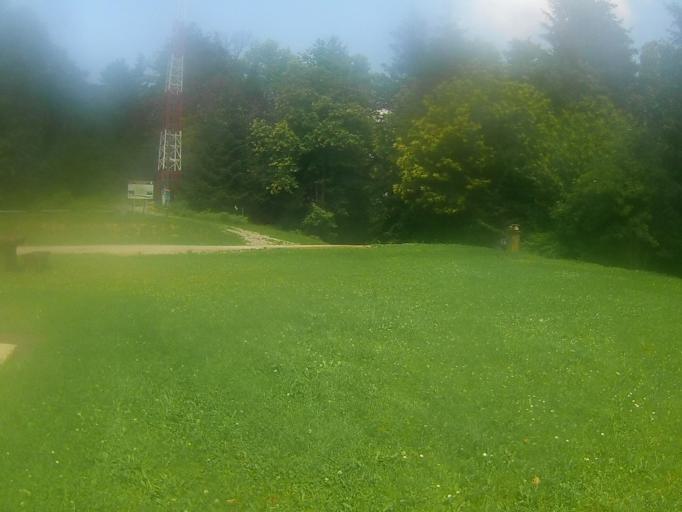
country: SI
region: Maribor
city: Bresternica
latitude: 46.6036
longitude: 15.5617
